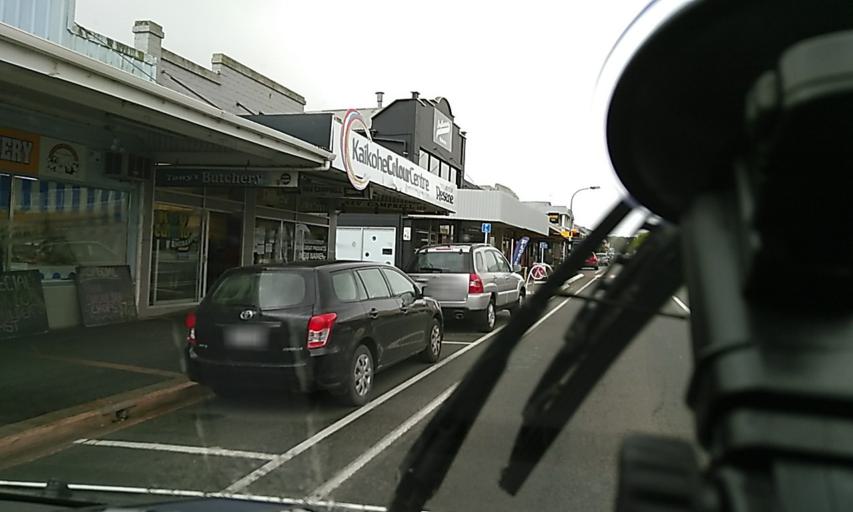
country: NZ
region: Northland
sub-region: Far North District
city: Waimate North
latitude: -35.4075
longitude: 173.8001
